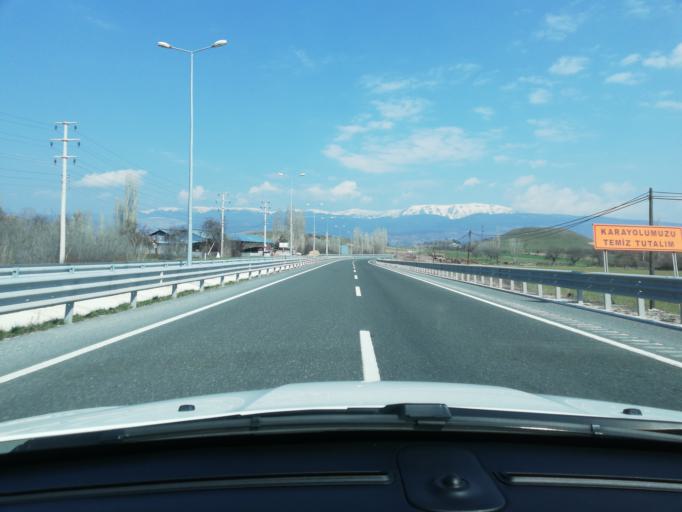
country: TR
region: Cankiri
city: Ilgaz
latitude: 40.9081
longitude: 33.6500
